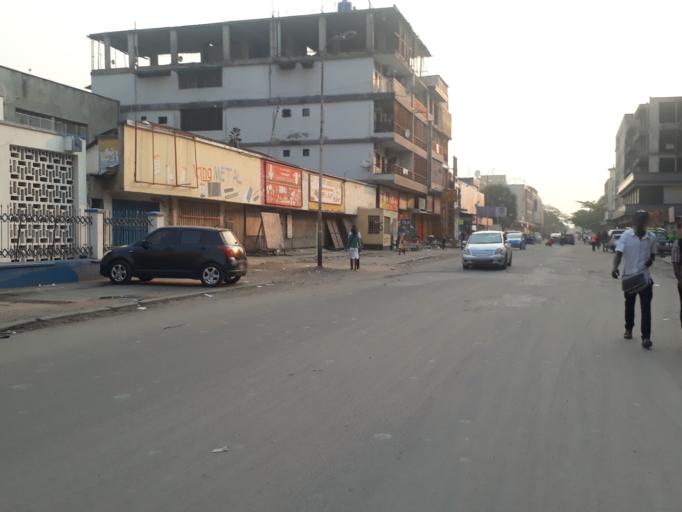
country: CD
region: Kinshasa
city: Kinshasa
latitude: -4.3059
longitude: 15.3123
